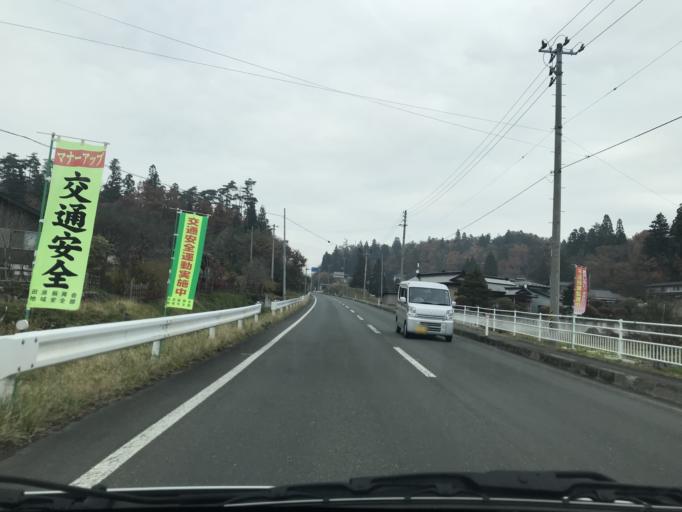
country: JP
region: Iwate
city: Mizusawa
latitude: 39.1618
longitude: 141.2019
